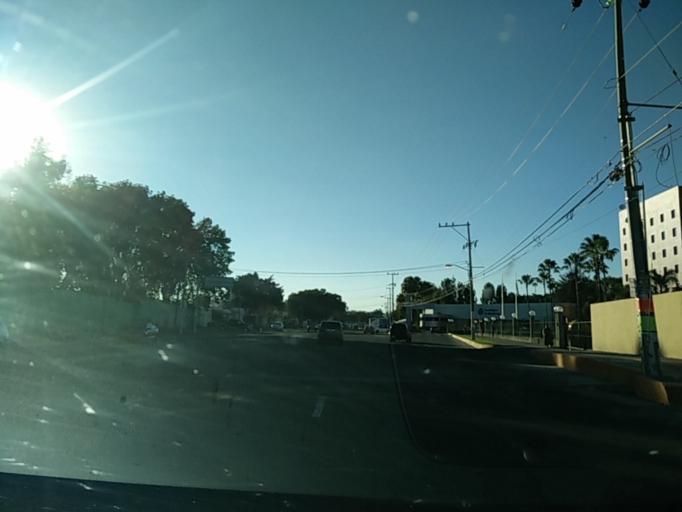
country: MX
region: Jalisco
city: Nuevo Mexico
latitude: 20.7313
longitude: -103.4525
